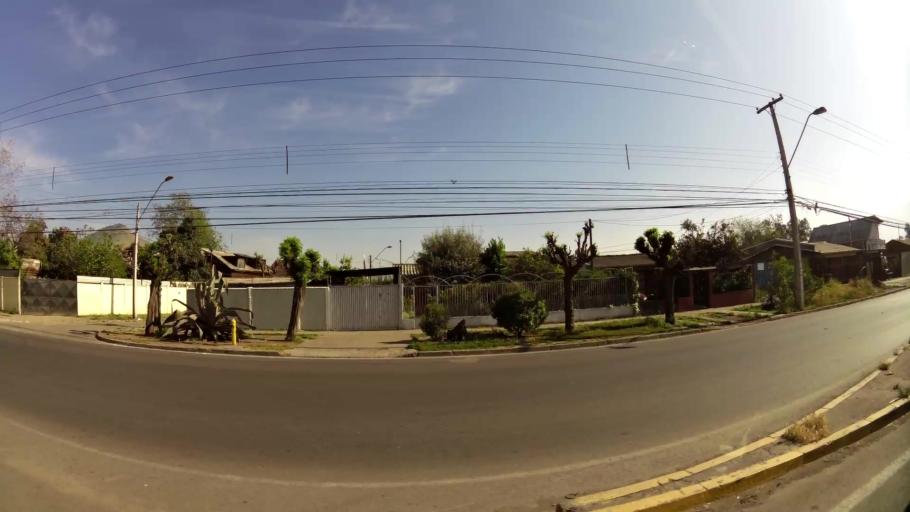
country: CL
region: Santiago Metropolitan
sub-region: Provincia de Santiago
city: Lo Prado
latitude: -33.3886
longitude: -70.6862
